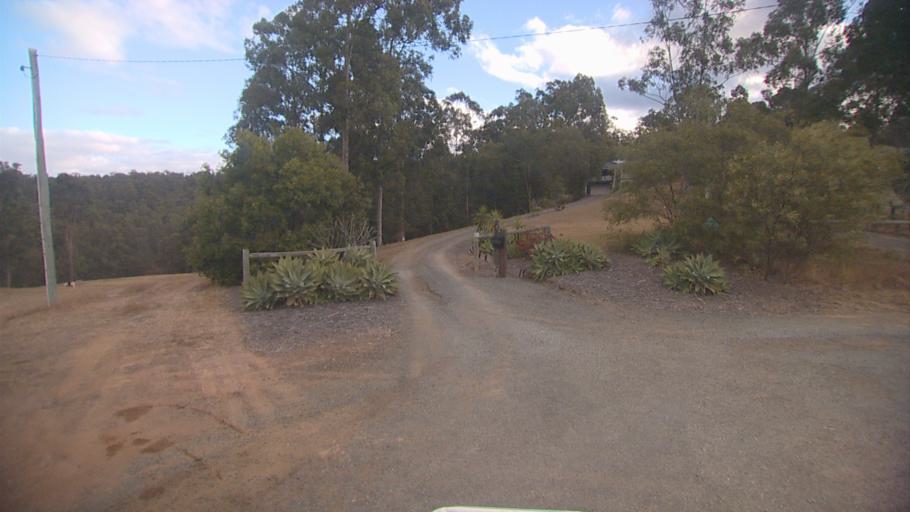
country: AU
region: Queensland
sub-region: Logan
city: Cedar Vale
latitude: -27.9308
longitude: 153.0503
